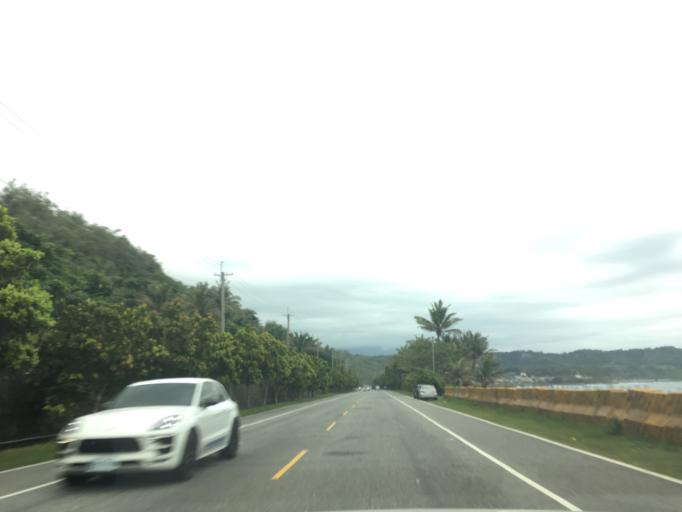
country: TW
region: Taiwan
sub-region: Taitung
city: Taitung
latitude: 23.1984
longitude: 121.3952
